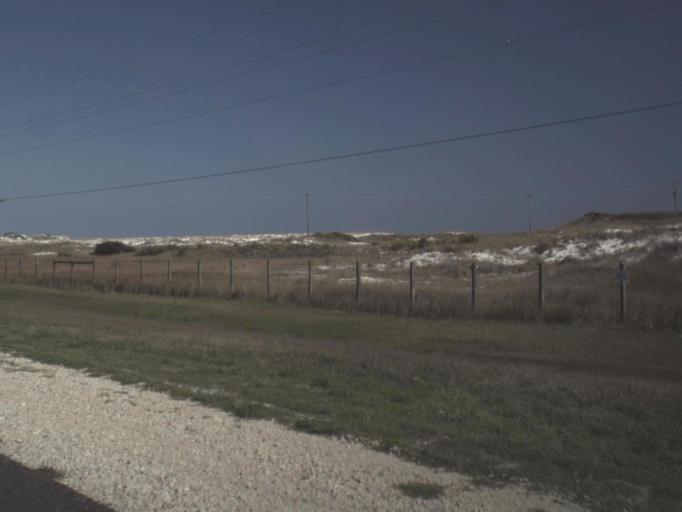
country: US
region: Florida
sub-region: Okaloosa County
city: Lake Lorraine
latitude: 30.3949
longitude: -86.5711
